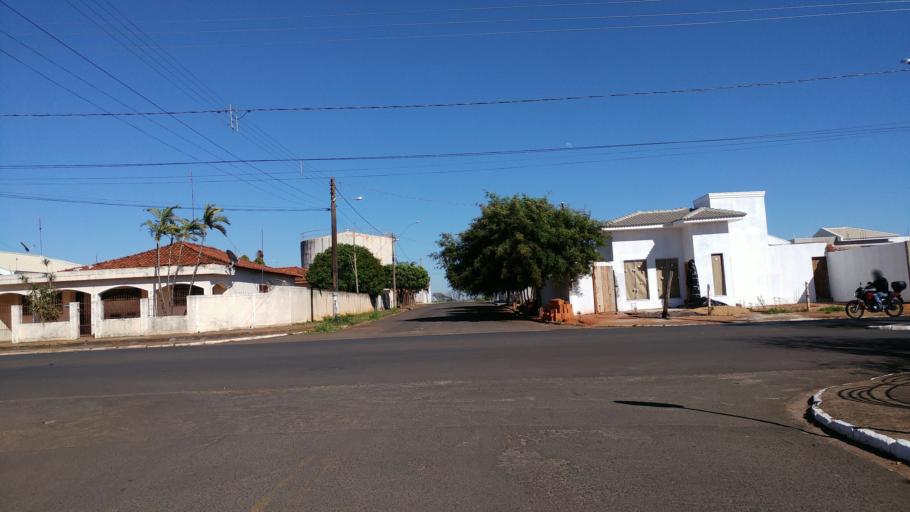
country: BR
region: Sao Paulo
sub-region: Paraguacu Paulista
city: Paraguacu Paulista
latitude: -22.4080
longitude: -50.5818
